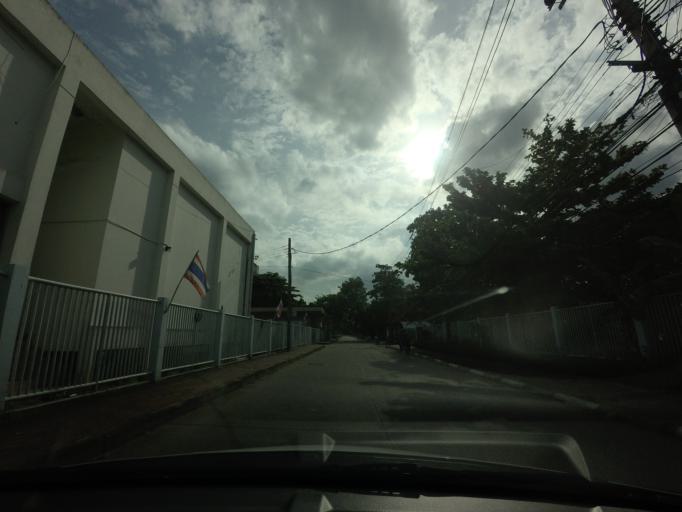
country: TH
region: Bangkok
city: Chatuchak
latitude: 13.8485
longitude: 100.5758
